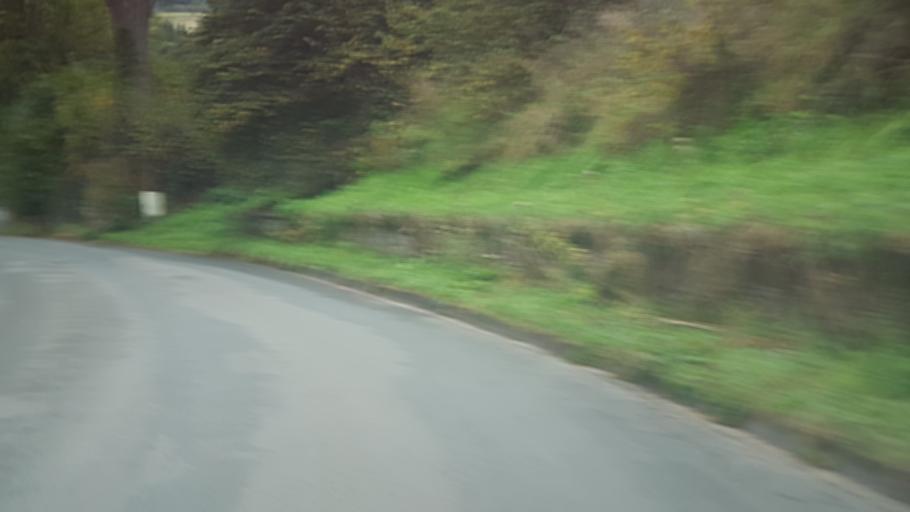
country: DE
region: North Rhine-Westphalia
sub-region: Regierungsbezirk Arnsberg
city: Herscheid
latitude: 51.2182
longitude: 7.6939
